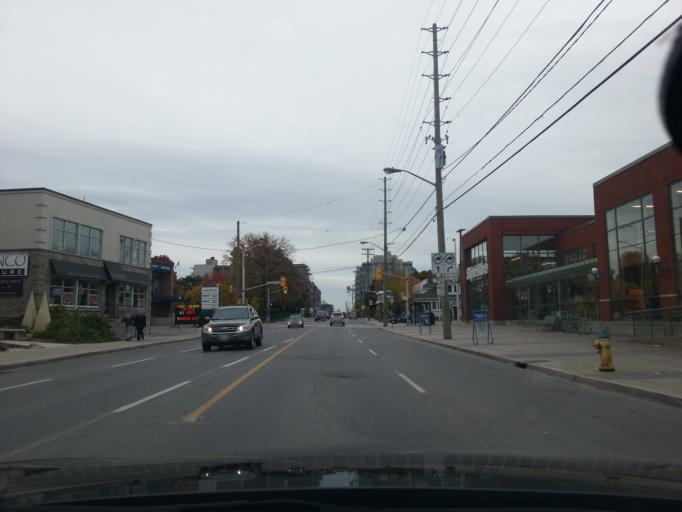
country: CA
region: Ontario
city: Ottawa
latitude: 45.3948
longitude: -75.7476
